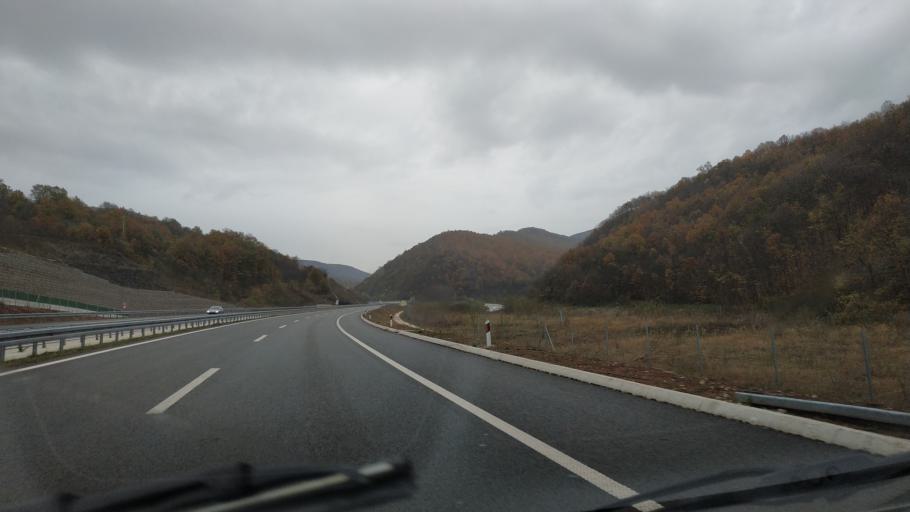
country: RS
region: Central Serbia
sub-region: Nisavski Okrug
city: Niska Banja
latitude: 43.2977
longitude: 22.0755
